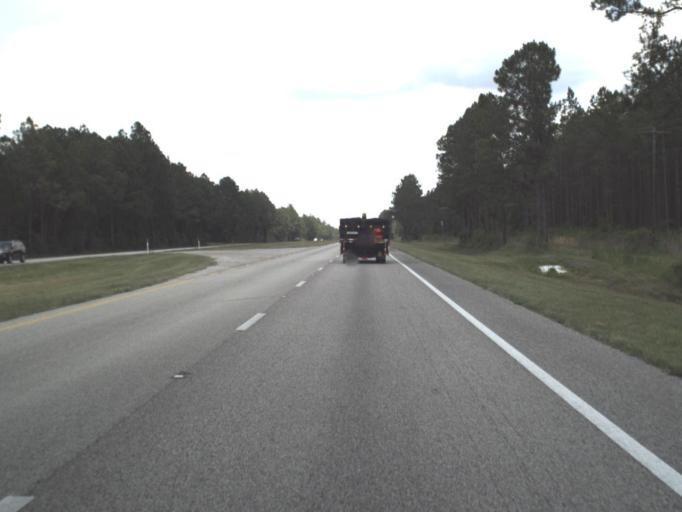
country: US
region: Florida
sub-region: Alachua County
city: Waldo
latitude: 29.7648
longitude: -82.2016
